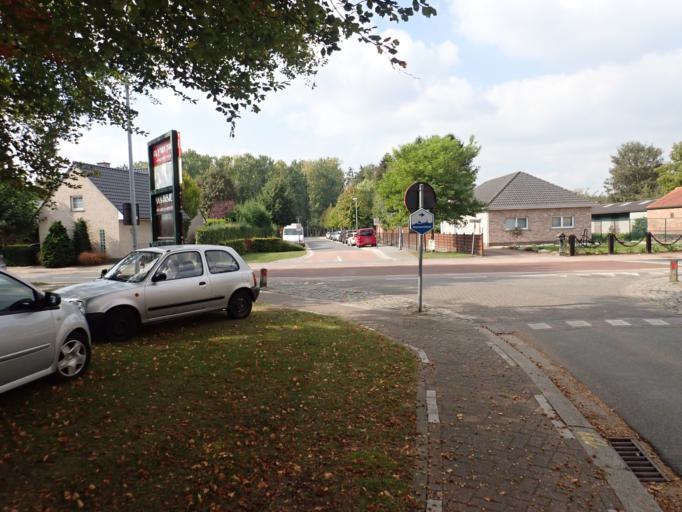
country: BE
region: Flanders
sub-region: Provincie Oost-Vlaanderen
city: Stekene
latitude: 51.2334
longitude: 4.0449
